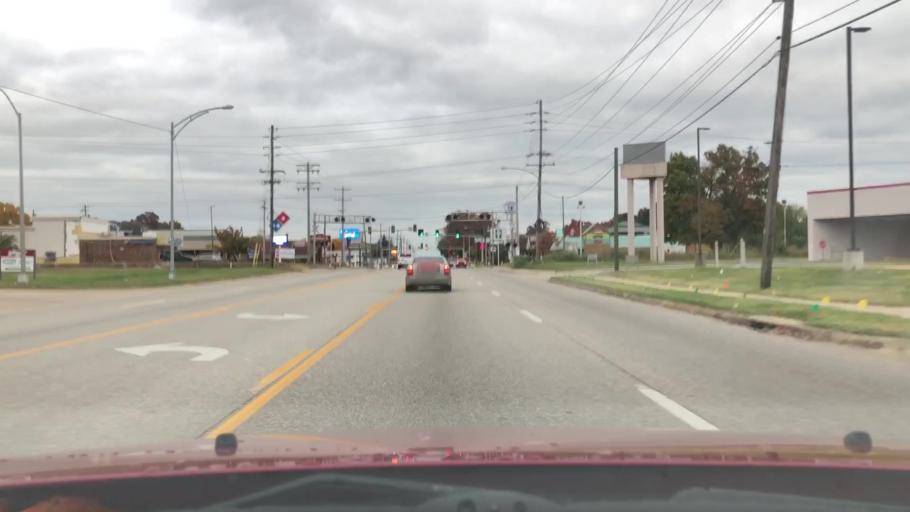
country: US
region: Missouri
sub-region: Greene County
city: Springfield
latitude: 37.1809
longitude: -93.2459
